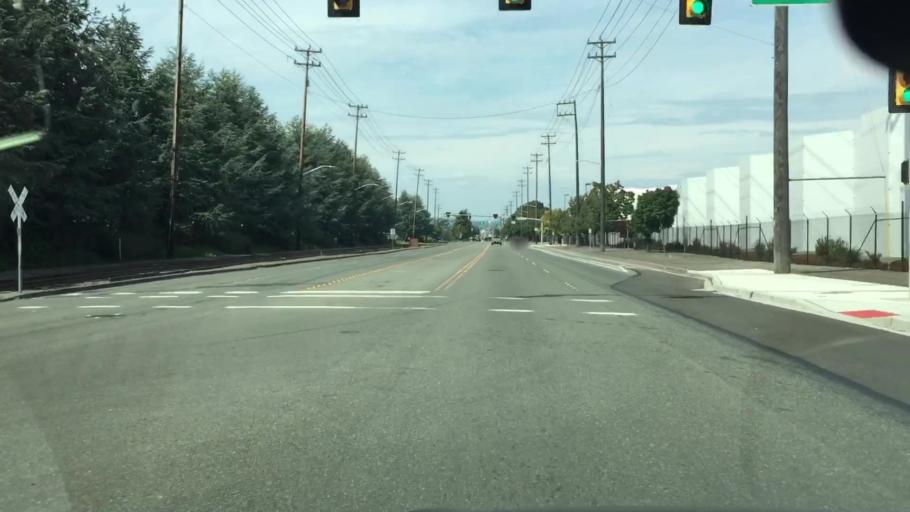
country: US
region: Washington
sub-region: King County
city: Boulevard Park
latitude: 47.5305
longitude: -122.3068
